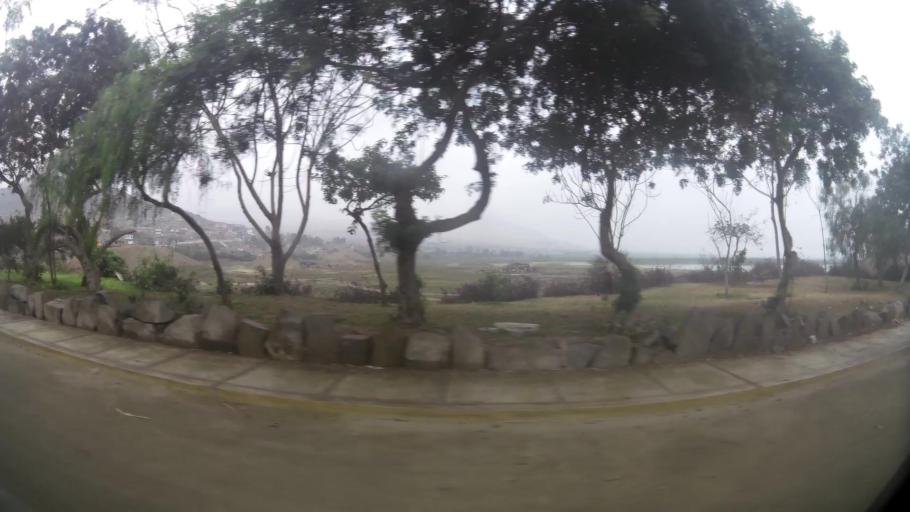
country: PE
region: Lima
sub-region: Provincia de Huaral
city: Chancay
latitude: -11.5902
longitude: -77.2712
